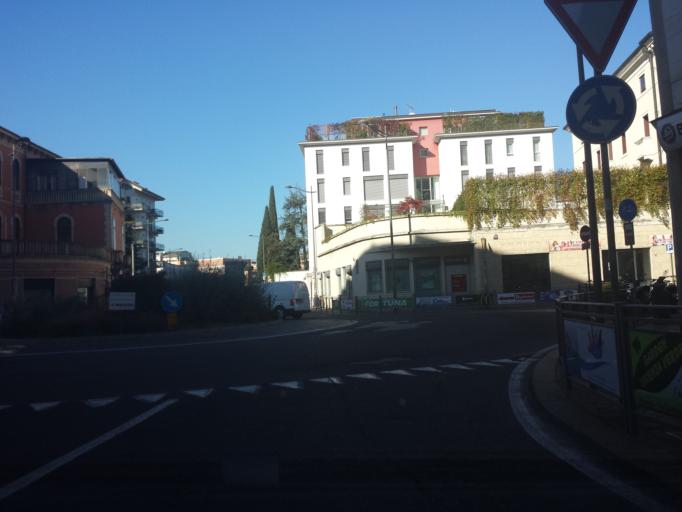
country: IT
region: Veneto
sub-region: Provincia di Vicenza
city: Vicenza
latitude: 45.5452
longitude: 11.5357
